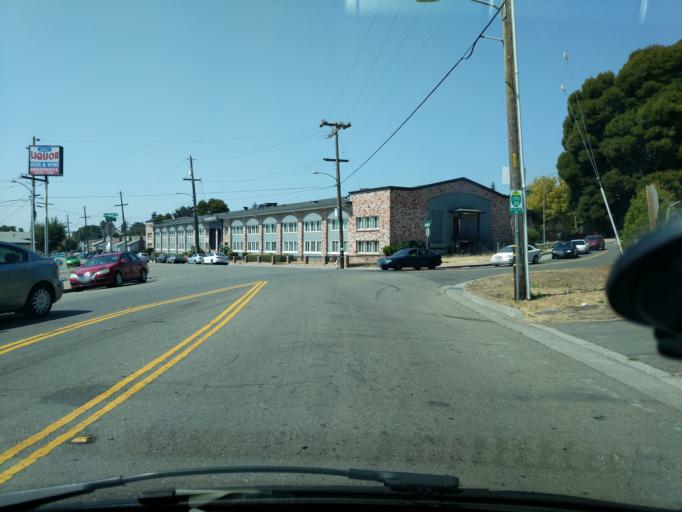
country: US
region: California
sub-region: Alameda County
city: San Leandro
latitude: 37.7449
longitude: -122.1498
